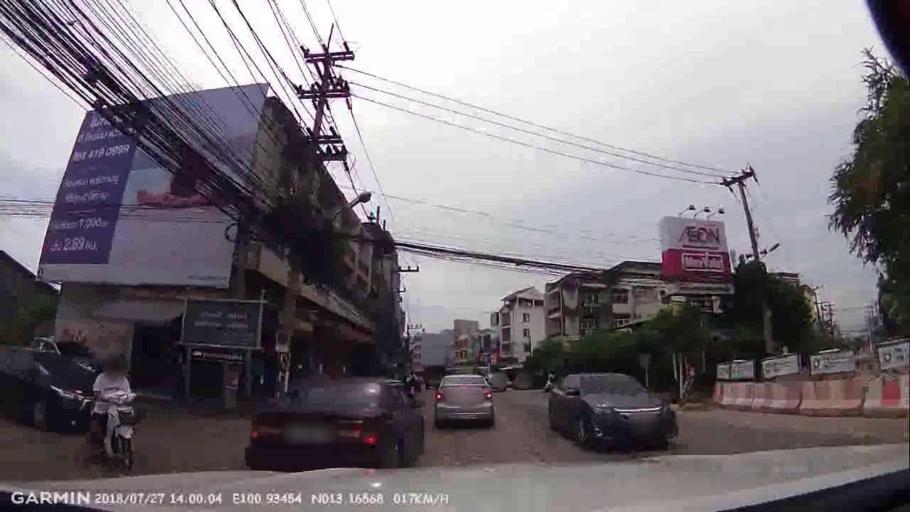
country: TH
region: Chon Buri
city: Si Racha
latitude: 13.1657
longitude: 100.9345
